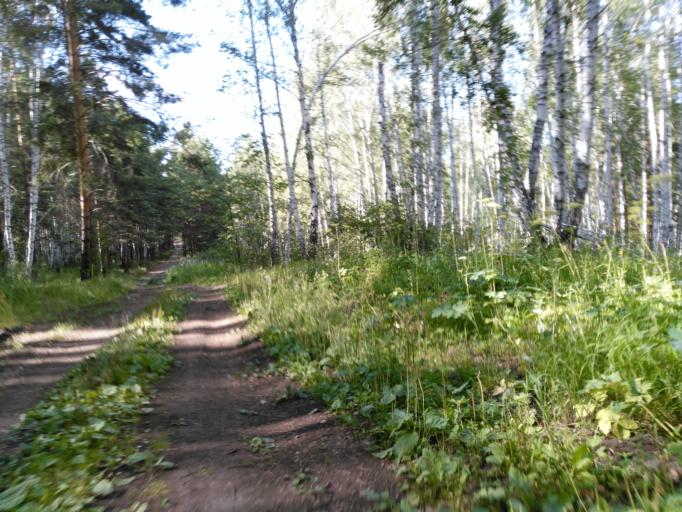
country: RU
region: Bashkortostan
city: Uchaly
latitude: 54.3324
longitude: 59.3574
